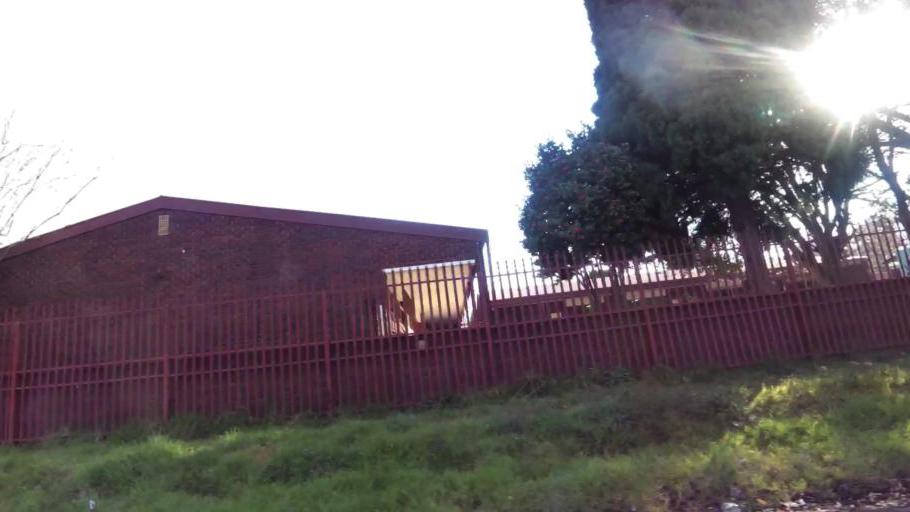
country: ZA
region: Gauteng
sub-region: City of Johannesburg Metropolitan Municipality
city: Johannesburg
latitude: -26.1939
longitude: 28.0190
